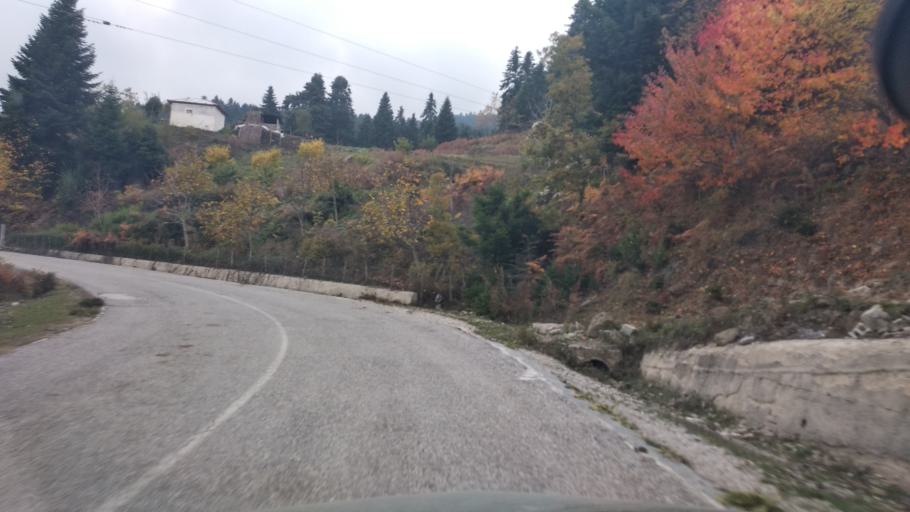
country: GR
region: Thessaly
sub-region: Trikala
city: Fiki
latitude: 39.5840
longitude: 21.4898
